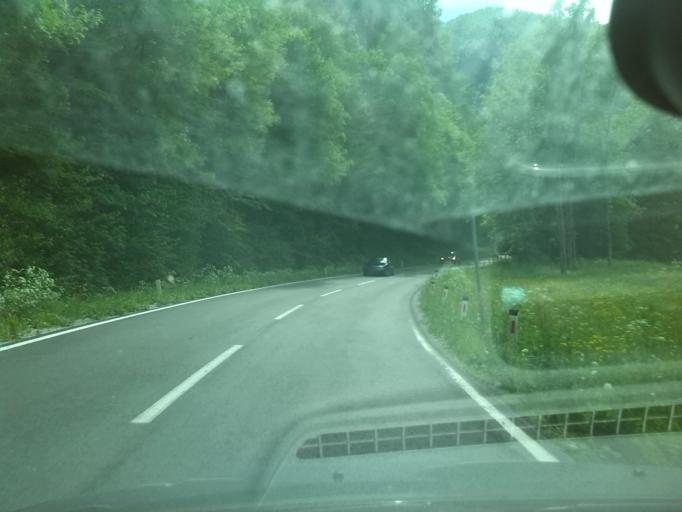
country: SI
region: Kobarid
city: Kobarid
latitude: 46.2433
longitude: 13.5110
